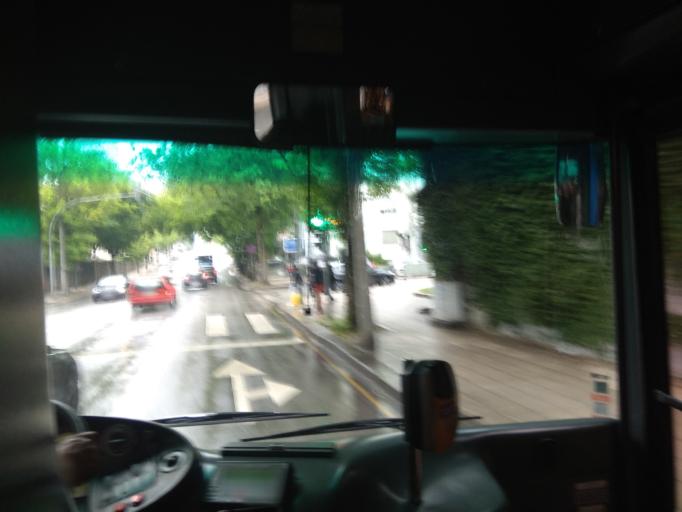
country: PT
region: Porto
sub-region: Porto
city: Porto
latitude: 41.1526
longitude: -8.6283
